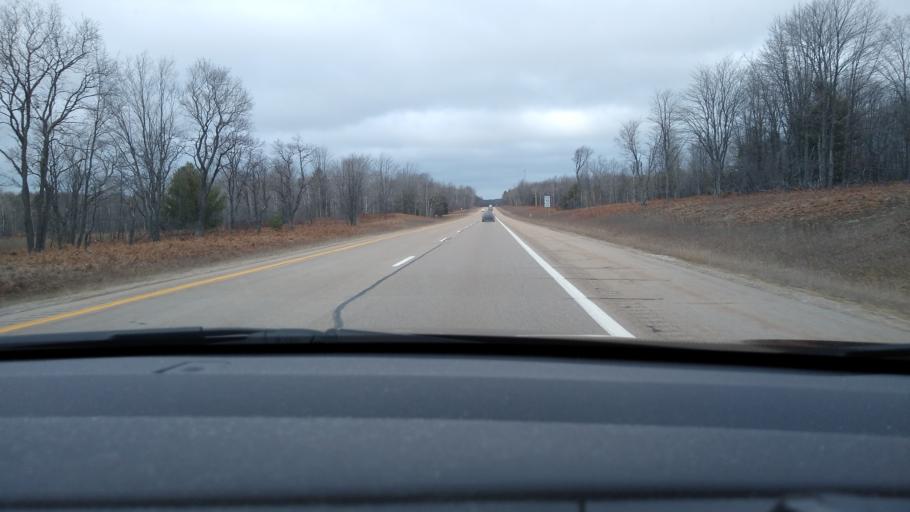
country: US
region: Michigan
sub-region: Crawford County
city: Grayling
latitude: 44.7950
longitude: -84.7137
